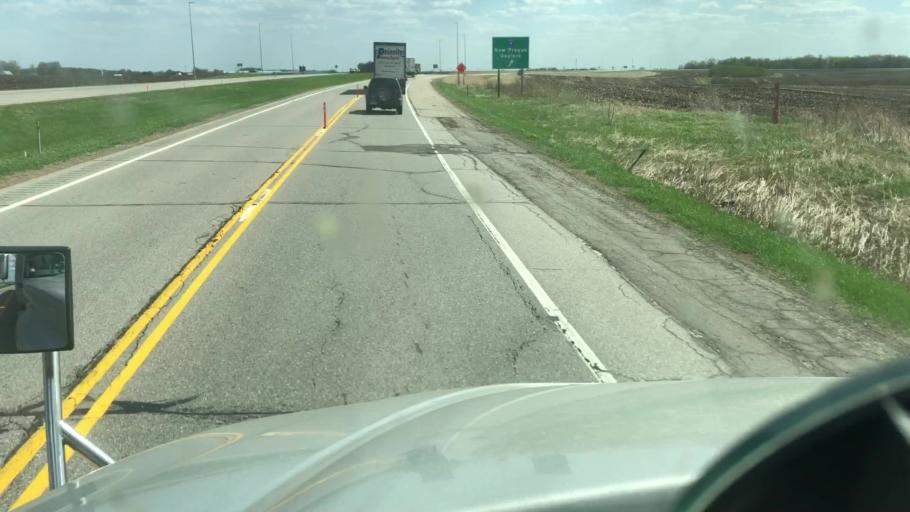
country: US
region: Minnesota
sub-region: Scott County
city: Belle Plaine
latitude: 44.5506
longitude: -93.8497
